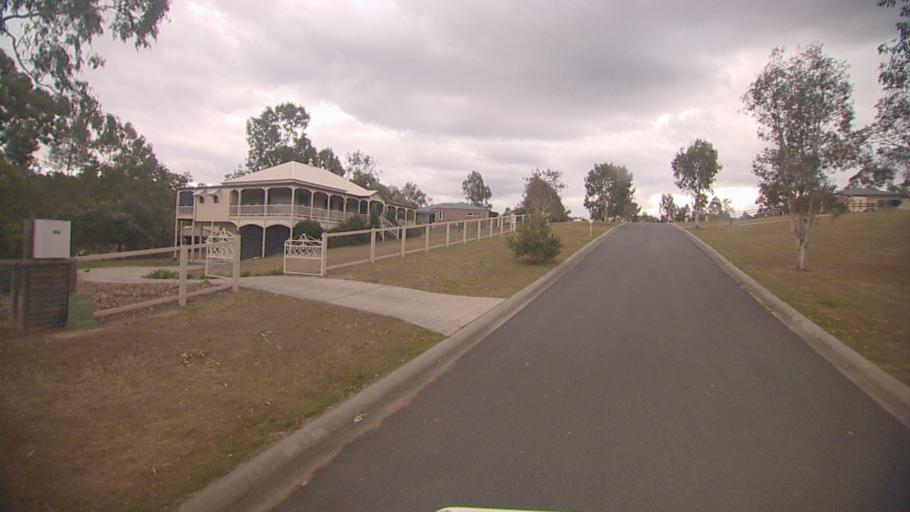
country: AU
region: Queensland
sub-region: Logan
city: Cedar Vale
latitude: -27.8708
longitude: 153.0784
